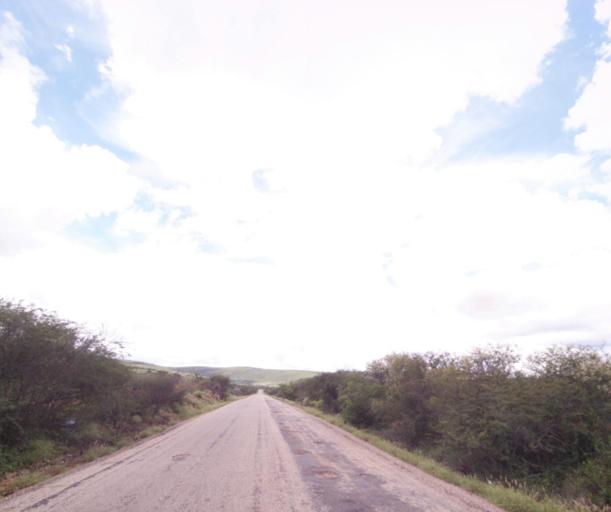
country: BR
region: Bahia
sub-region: Brumado
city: Brumado
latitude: -14.1865
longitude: -41.5743
